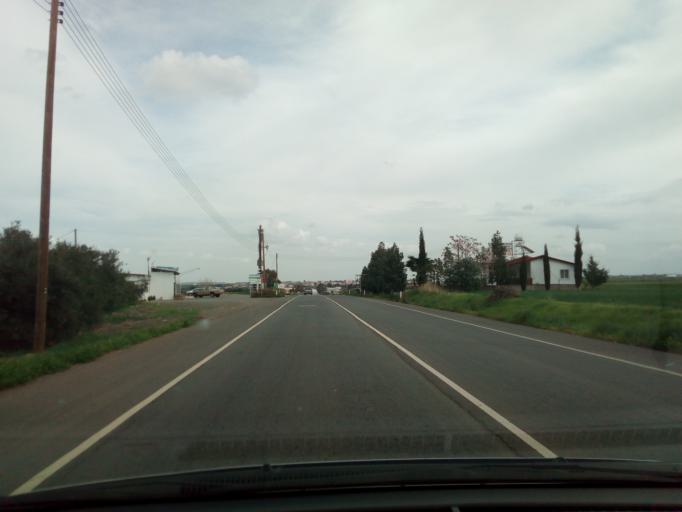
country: CY
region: Lefkosia
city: Akaki
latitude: 35.1352
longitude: 33.1036
